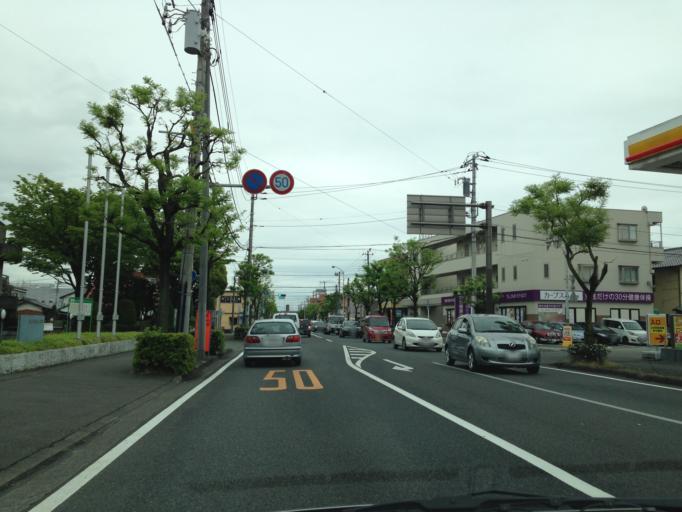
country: JP
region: Shizuoka
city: Fuji
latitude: 35.1594
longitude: 138.6855
